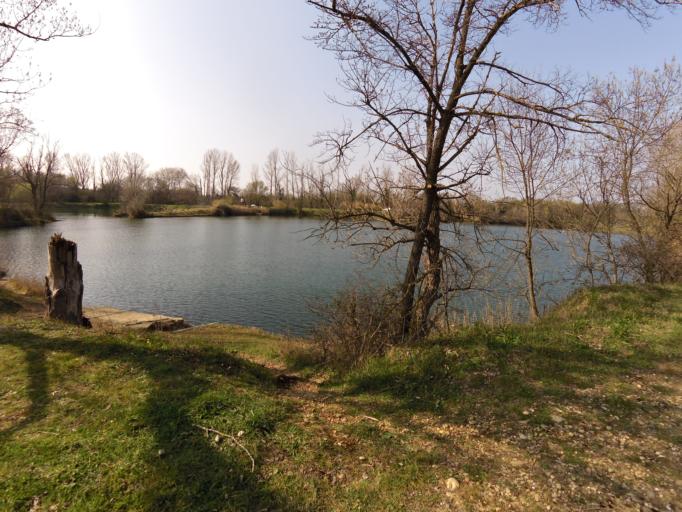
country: FR
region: Languedoc-Roussillon
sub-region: Departement du Gard
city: Vestric-et-Candiac
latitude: 43.7261
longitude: 4.2650
